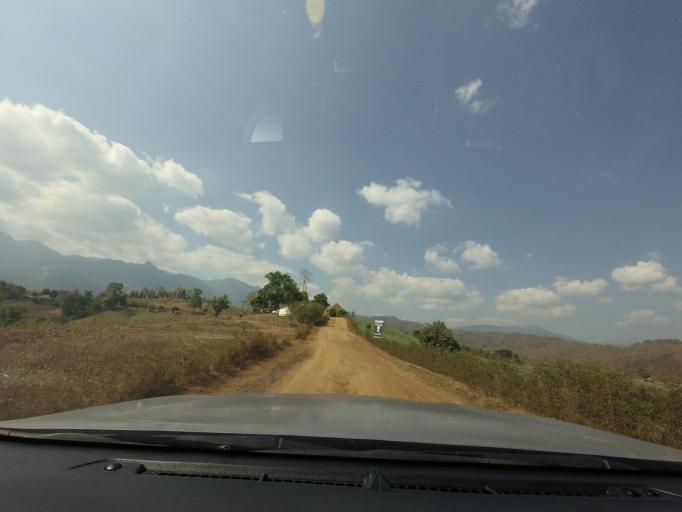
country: TH
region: Mae Hong Son
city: Wiang Nuea
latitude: 19.4003
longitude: 98.4100
